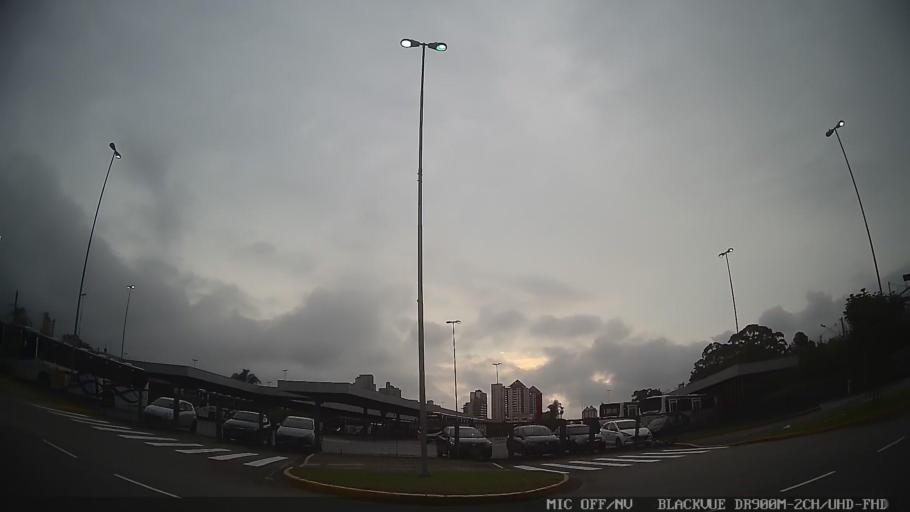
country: BR
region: Sao Paulo
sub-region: Mogi das Cruzes
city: Mogi das Cruzes
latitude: -23.5165
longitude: -46.1845
